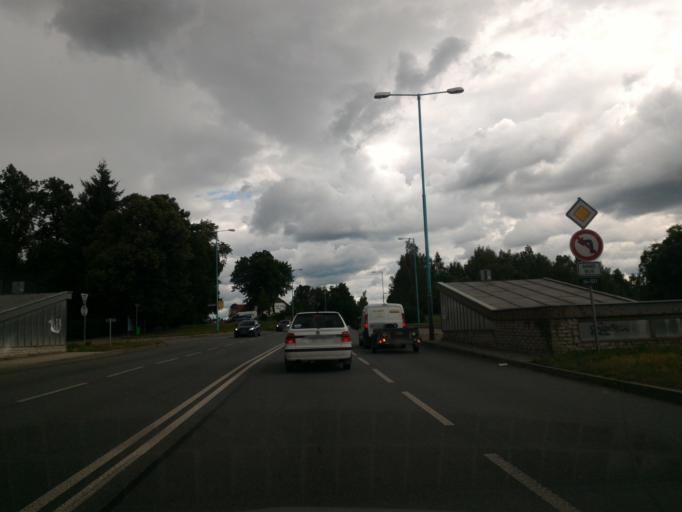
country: CZ
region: Vysocina
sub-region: Okres Pelhrimov
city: Pelhrimov
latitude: 49.4250
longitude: 15.2246
